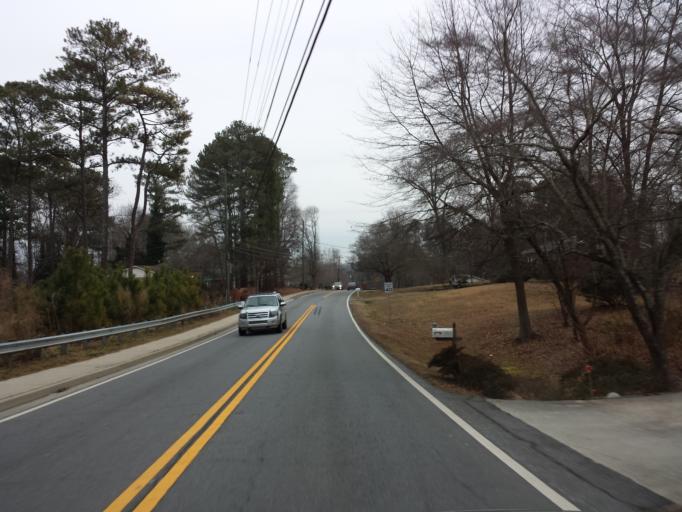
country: US
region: Georgia
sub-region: Fulton County
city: Roswell
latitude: 34.0116
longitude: -84.4549
